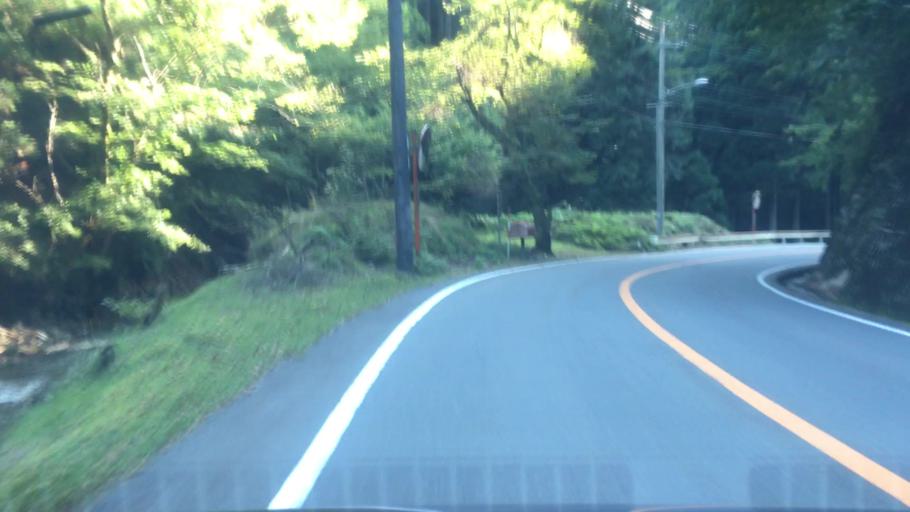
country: JP
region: Hyogo
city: Toyooka
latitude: 35.6169
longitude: 134.8583
